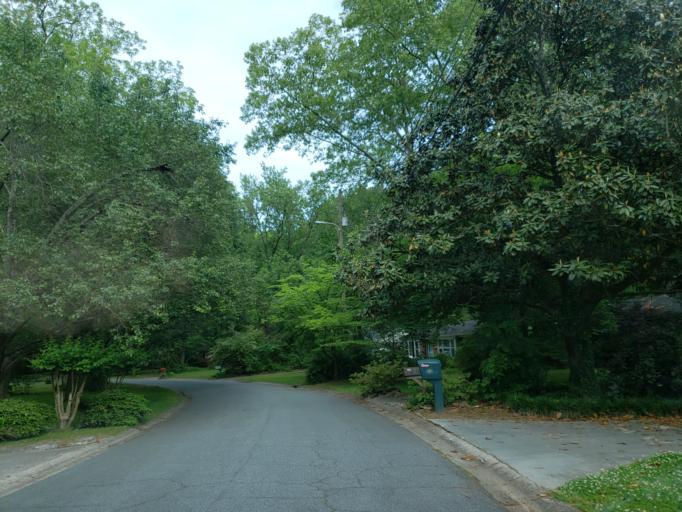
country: US
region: Georgia
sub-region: Cobb County
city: Marietta
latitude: 33.9460
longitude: -84.5673
